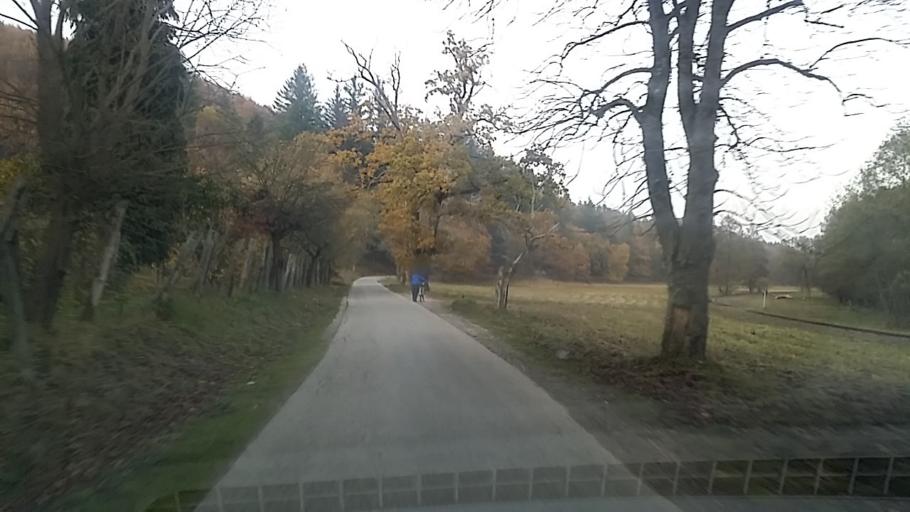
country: HU
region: Borsod-Abauj-Zemplen
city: Tolcsva
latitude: 48.4481
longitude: 21.4631
